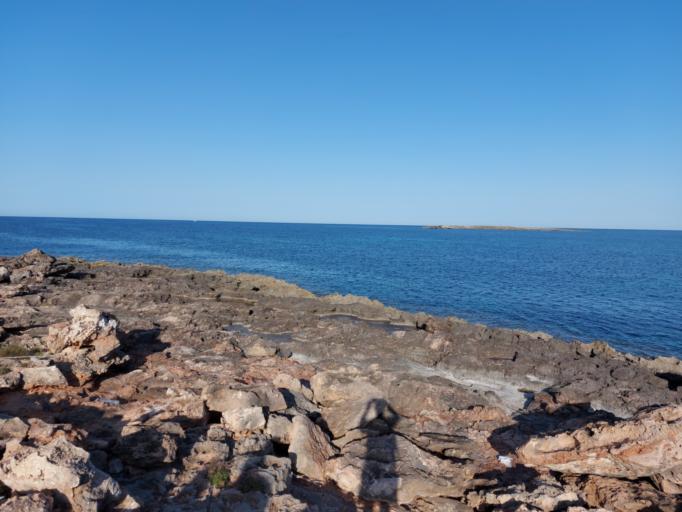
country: ES
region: Balearic Islands
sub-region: Illes Balears
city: Ses Salines
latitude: 39.2992
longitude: 3.0178
